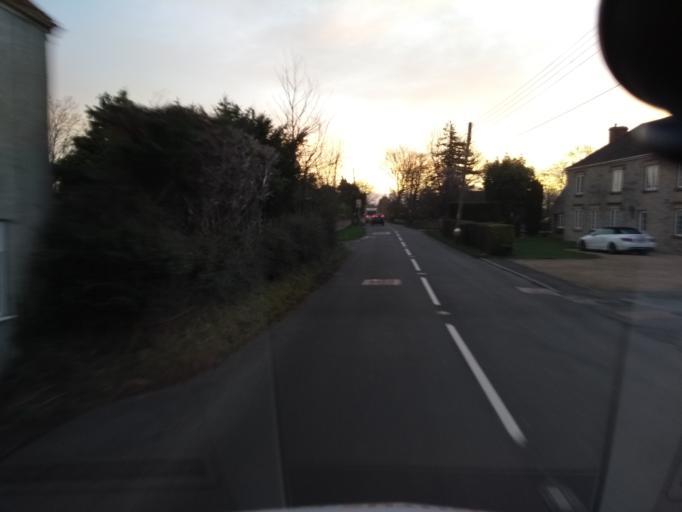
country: GB
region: England
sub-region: Somerset
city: Woolavington
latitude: 51.2255
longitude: -2.9023
